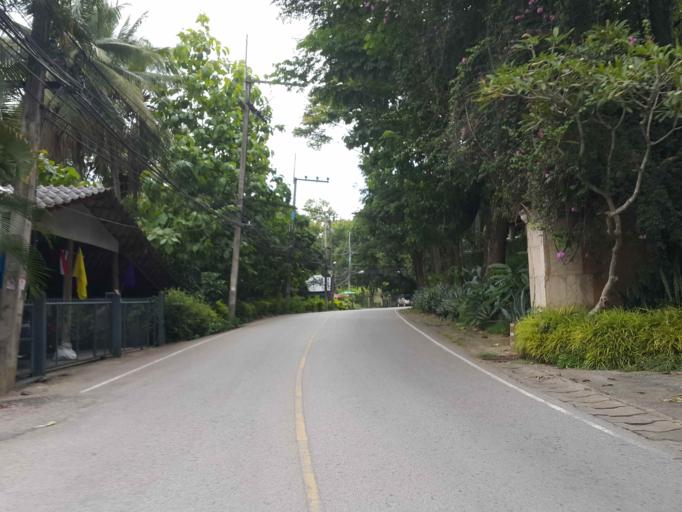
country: TH
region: Chiang Mai
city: San Sai
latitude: 18.9150
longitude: 98.9291
